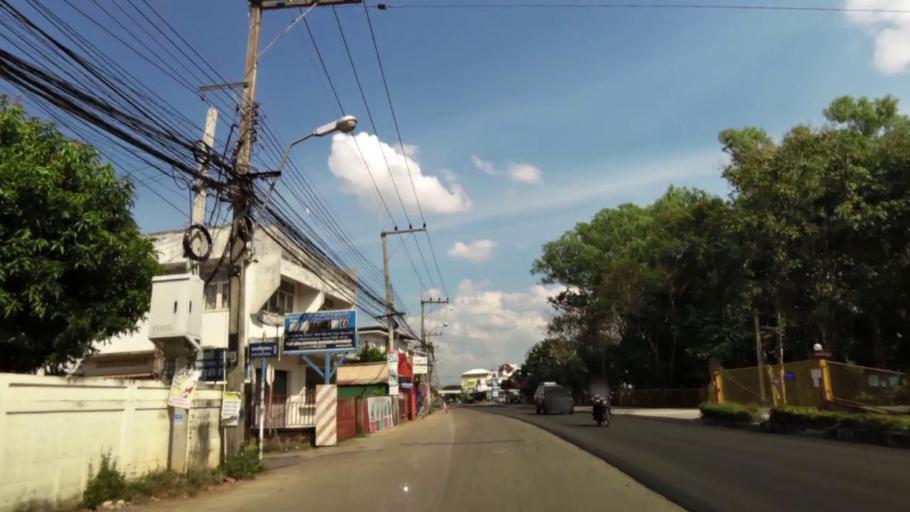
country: TH
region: Phrae
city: Phrae
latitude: 18.1346
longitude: 100.1386
